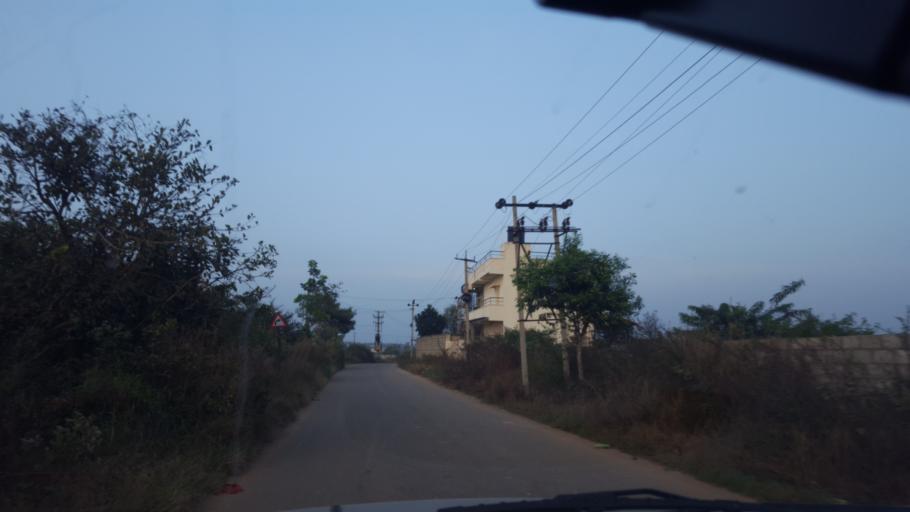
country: IN
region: Karnataka
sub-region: Bangalore Urban
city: Yelahanka
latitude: 13.0737
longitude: 77.6903
